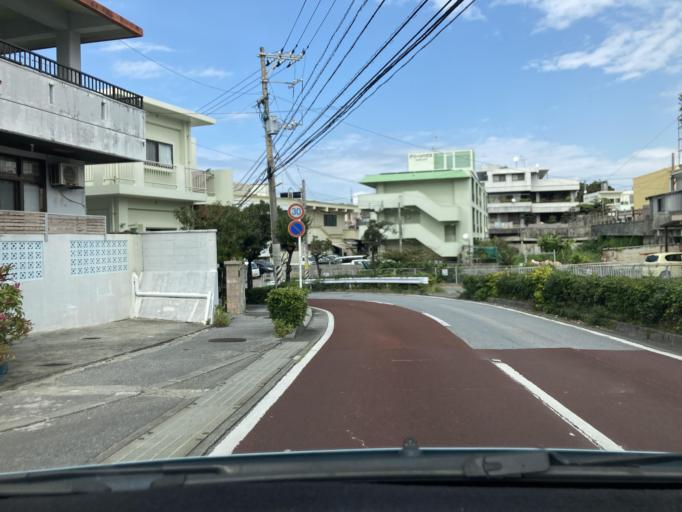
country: JP
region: Okinawa
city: Tomigusuku
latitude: 26.1900
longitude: 127.6934
